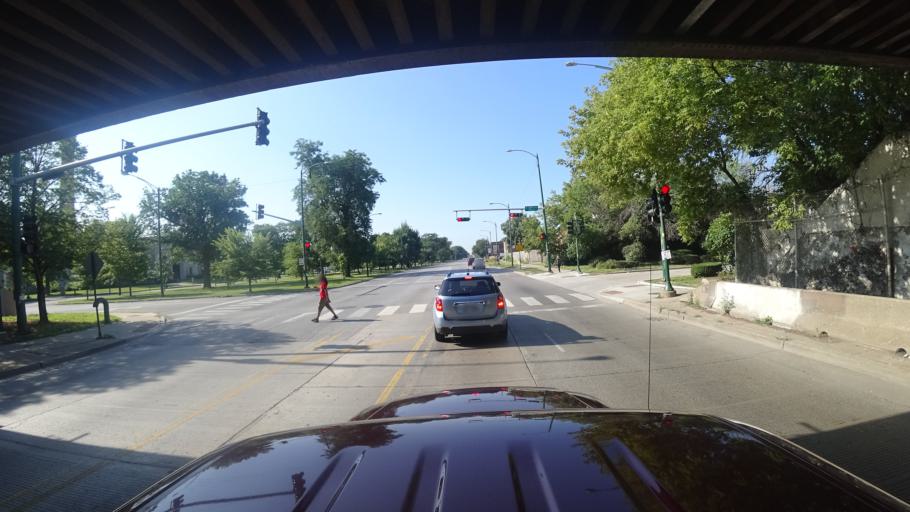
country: US
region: Illinois
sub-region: Cook County
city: Chicago
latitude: 41.8044
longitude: -87.6844
